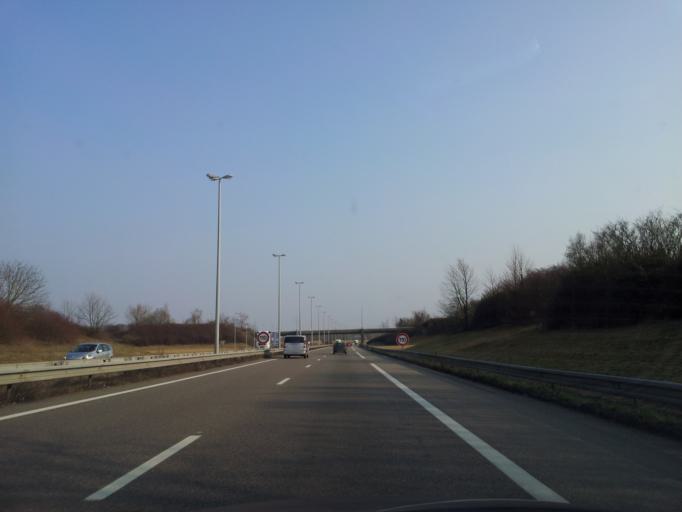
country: FR
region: Alsace
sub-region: Departement du Haut-Rhin
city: Hesingue
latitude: 47.6030
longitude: 7.5332
